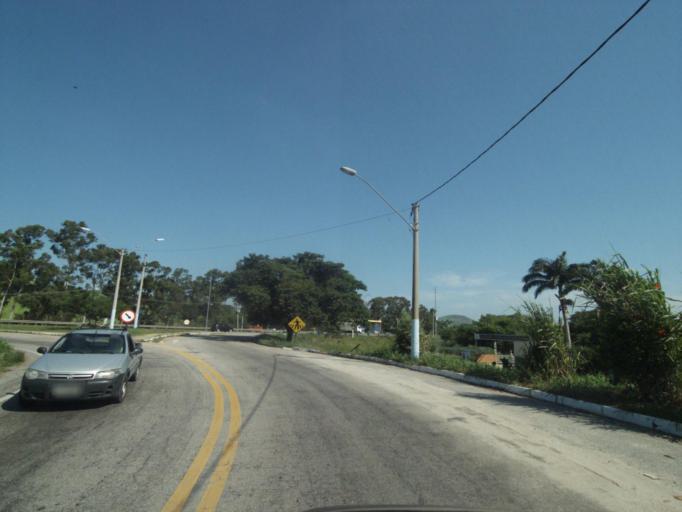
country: BR
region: Rio de Janeiro
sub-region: Niteroi
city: Niteroi
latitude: -22.8455
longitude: -43.0992
